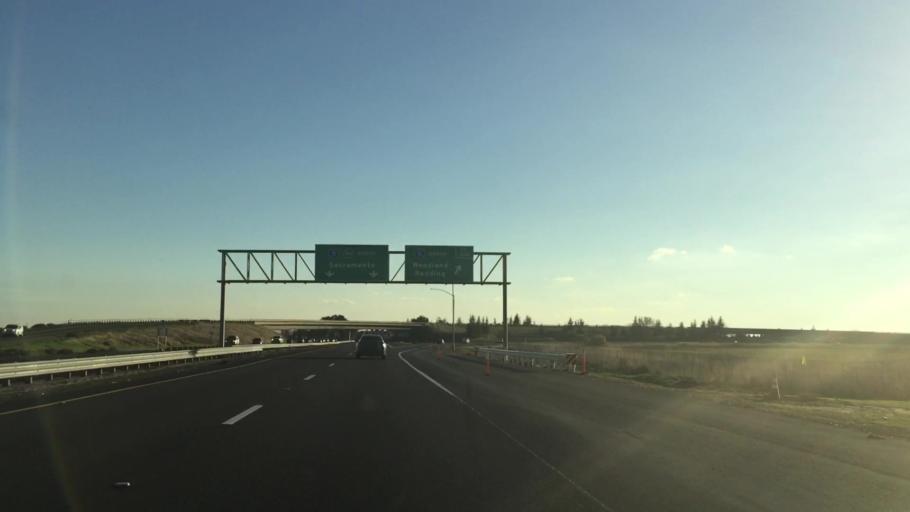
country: US
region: California
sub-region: Sacramento County
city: Elverta
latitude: 38.6744
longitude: -121.5402
